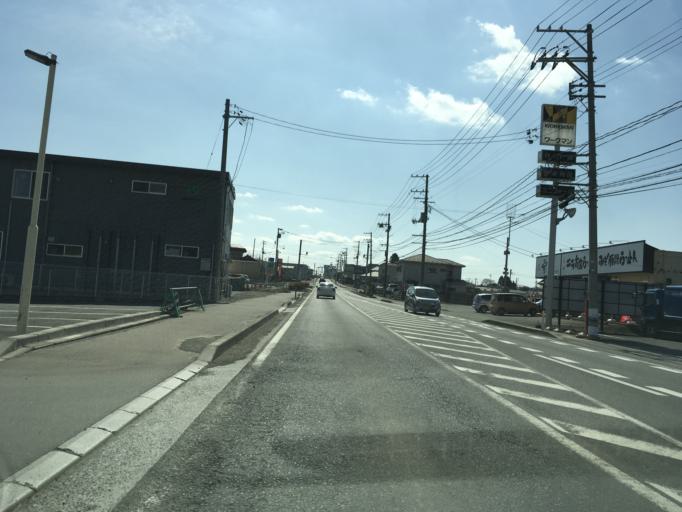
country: JP
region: Iwate
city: Ofunato
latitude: 38.8422
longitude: 141.5807
